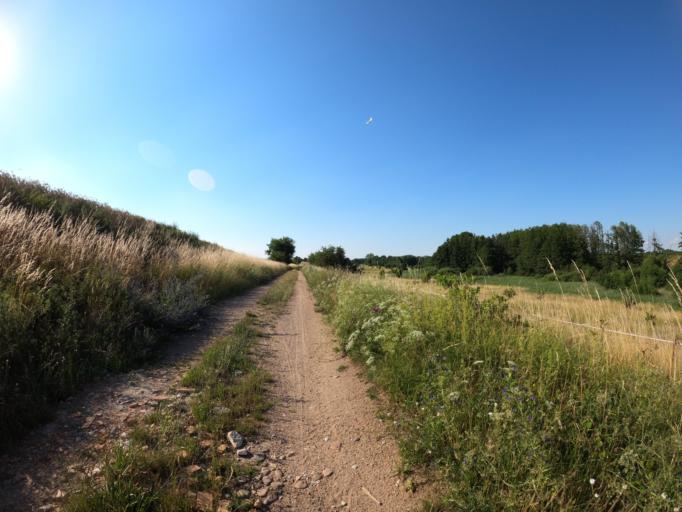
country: DE
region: Brandenburg
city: Gartz
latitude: 53.2238
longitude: 14.3711
